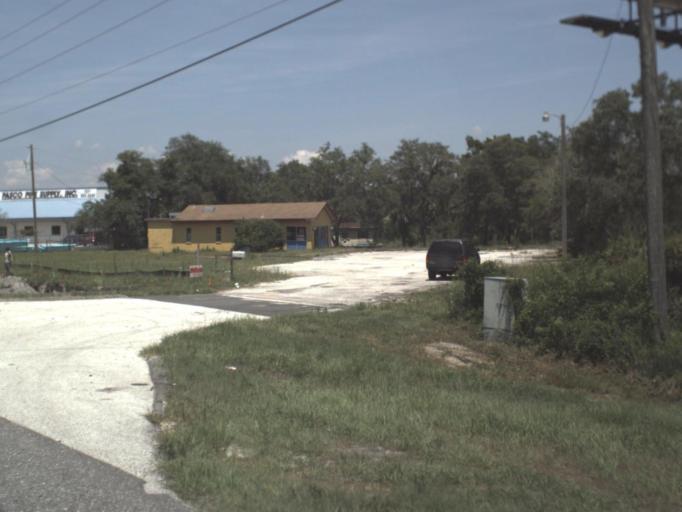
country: US
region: Florida
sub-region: Pasco County
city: Hudson
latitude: 28.3701
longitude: -82.6873
